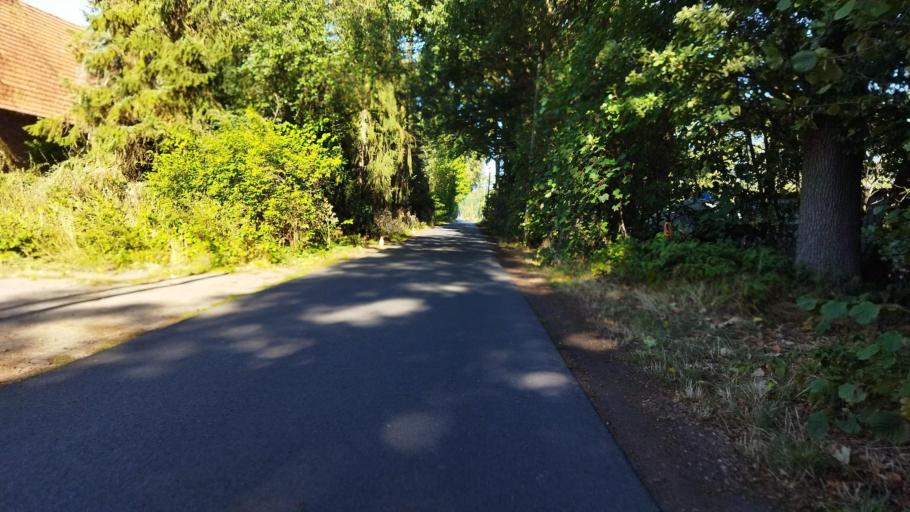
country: DE
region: North Rhine-Westphalia
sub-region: Regierungsbezirk Munster
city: Wettringen
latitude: 52.2297
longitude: 7.3202
